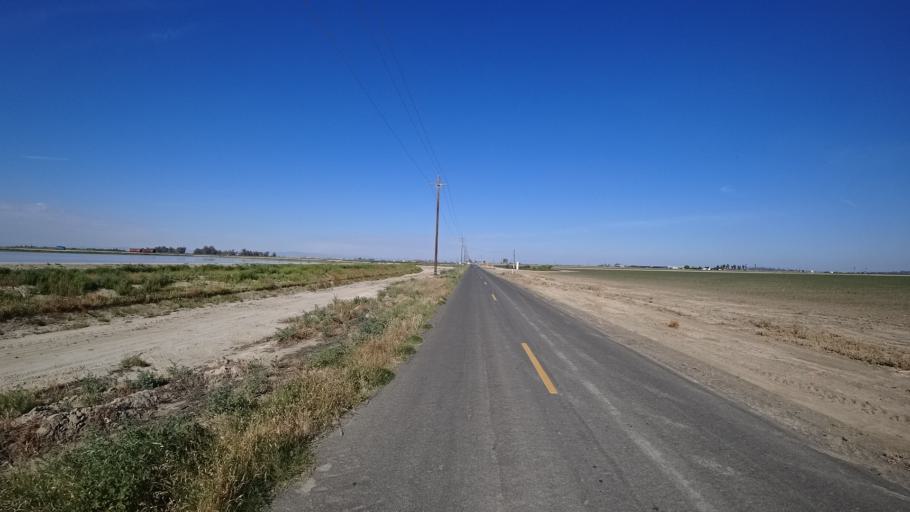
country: US
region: California
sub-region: Kings County
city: Home Garden
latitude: 36.2258
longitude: -119.6425
